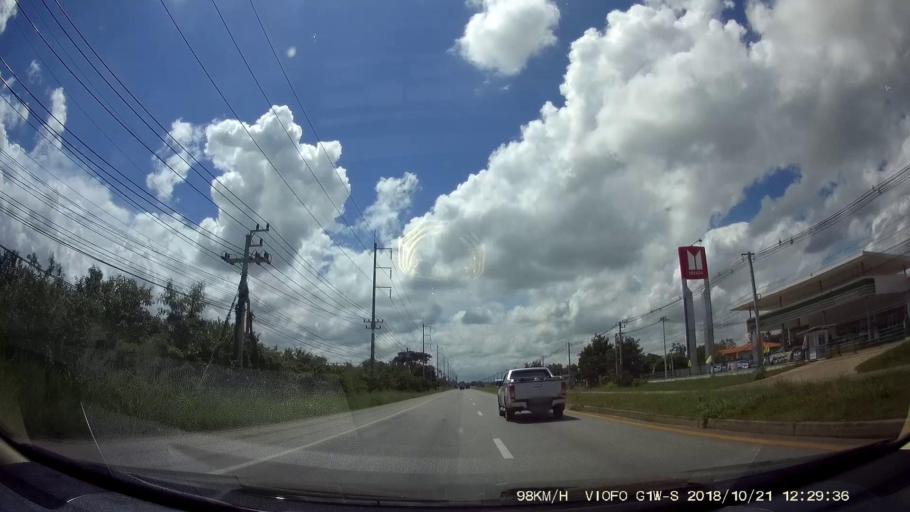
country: TH
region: Nakhon Ratchasima
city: Dan Khun Thot
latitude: 15.1795
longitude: 101.7481
